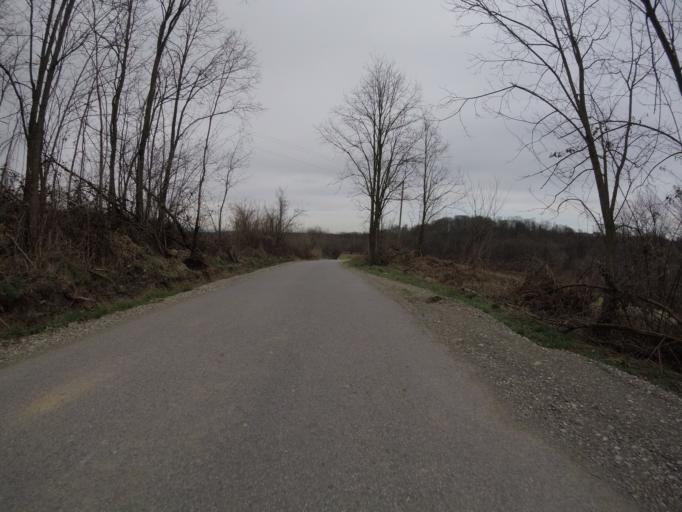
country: HR
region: Grad Zagreb
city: Strmec
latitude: 45.6674
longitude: 15.8834
